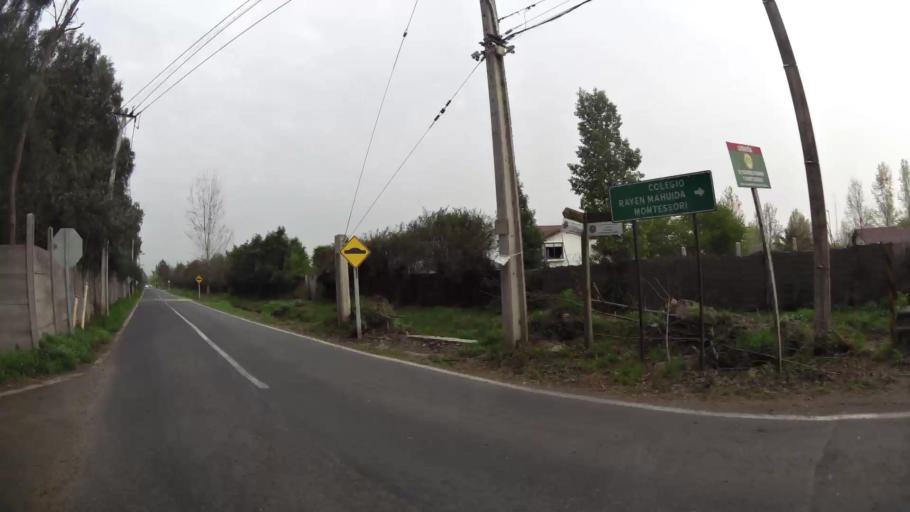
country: CL
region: Santiago Metropolitan
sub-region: Provincia de Chacabuco
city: Chicureo Abajo
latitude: -33.2704
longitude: -70.7109
